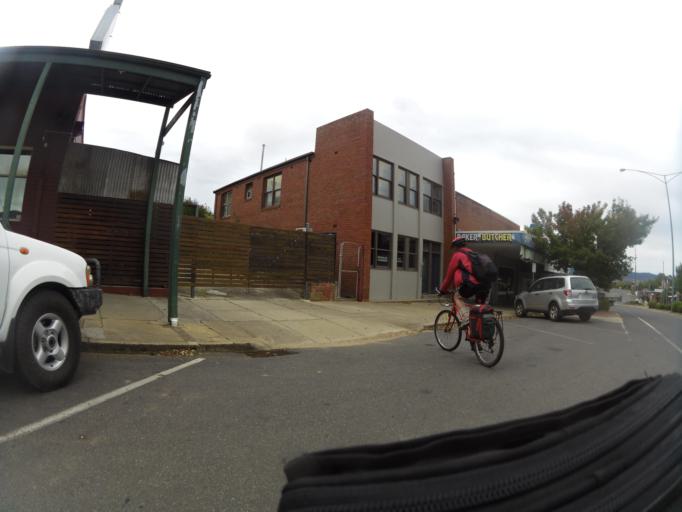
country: AU
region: New South Wales
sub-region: Snowy River
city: Jindabyne
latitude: -36.1954
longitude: 147.9054
